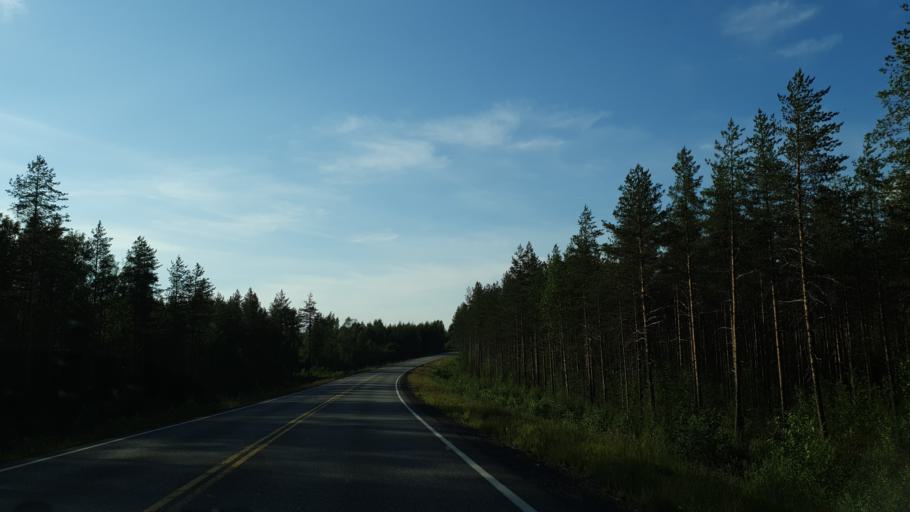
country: FI
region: Kainuu
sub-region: Kehys-Kainuu
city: Kuhmo
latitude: 64.0773
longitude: 29.4889
